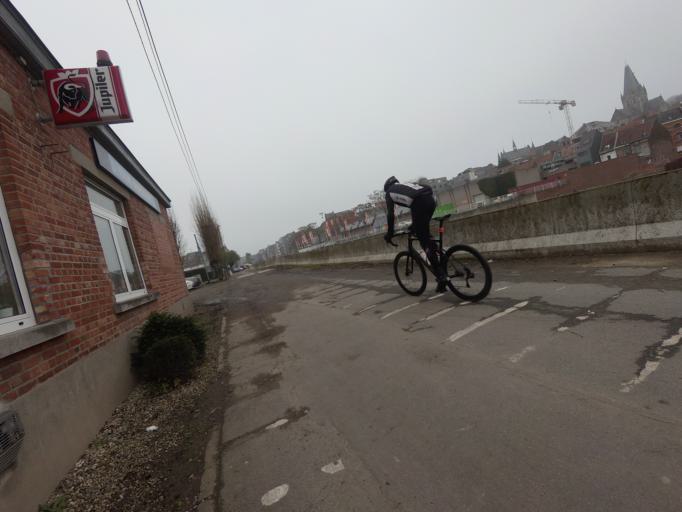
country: BE
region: Flanders
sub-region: Provincie Oost-Vlaanderen
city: Geraardsbergen
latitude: 50.7700
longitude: 3.8802
